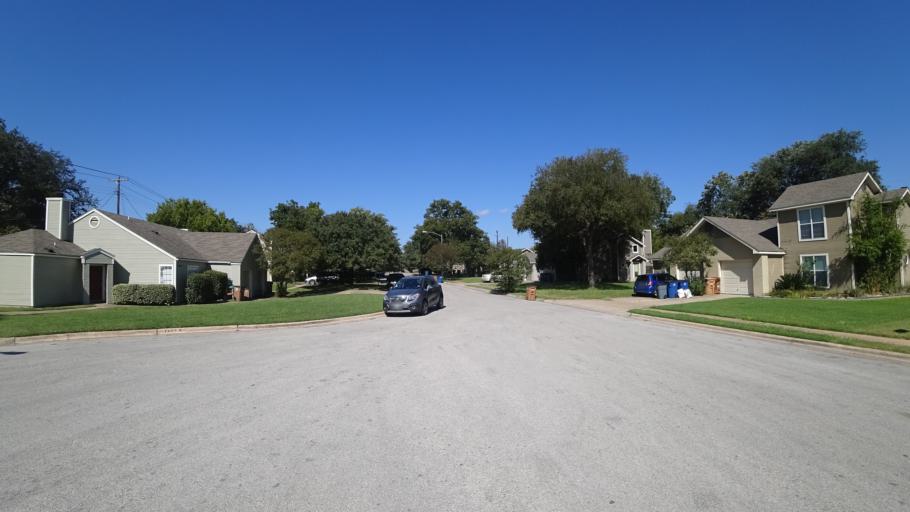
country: US
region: Texas
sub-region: Travis County
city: Austin
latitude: 30.3157
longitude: -97.6997
